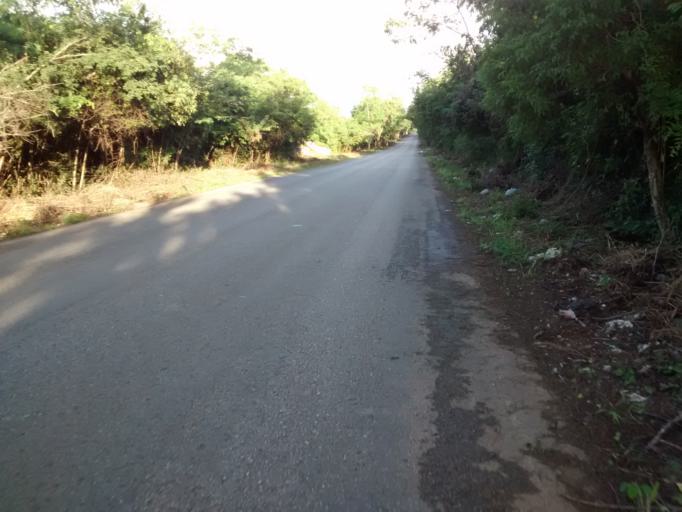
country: MX
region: Yucatan
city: Valladolid
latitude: 20.7313
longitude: -88.2265
